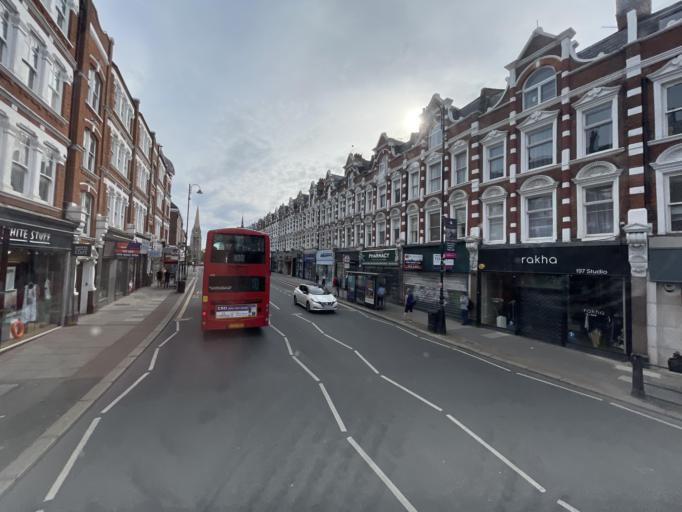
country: GB
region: England
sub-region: Greater London
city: Crouch End
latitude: 51.5909
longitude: -0.1426
